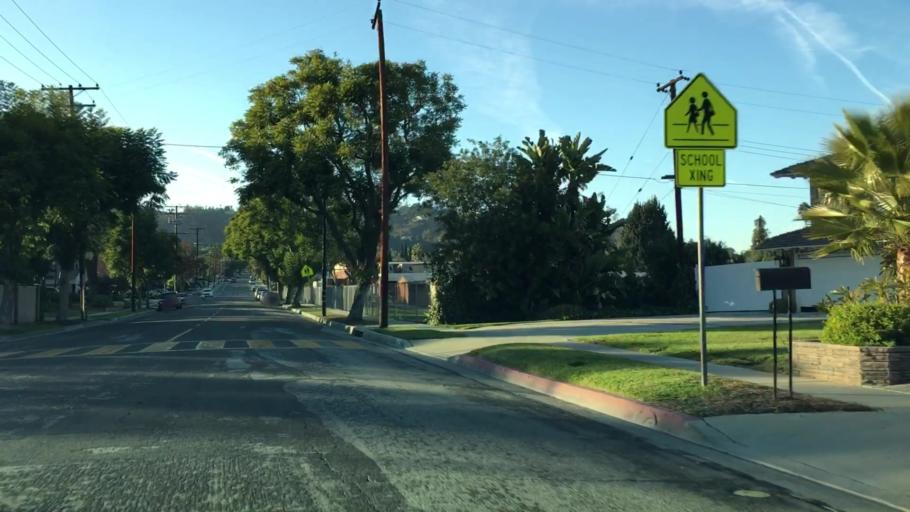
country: US
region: California
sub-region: Los Angeles County
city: Hacienda Heights
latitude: 33.9876
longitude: -117.9761
